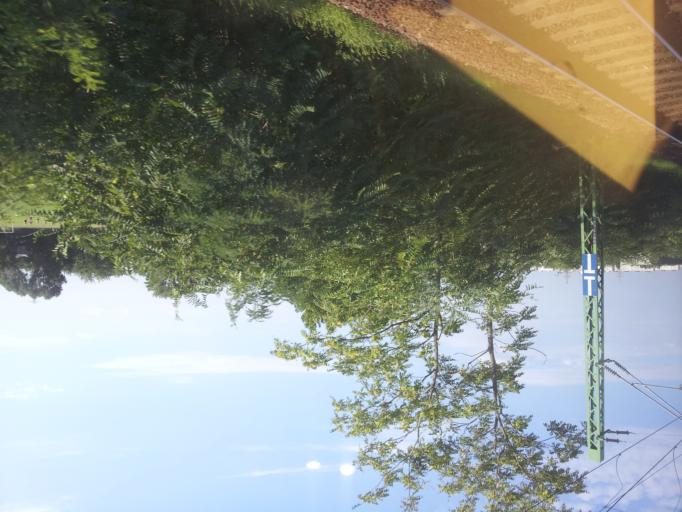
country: HU
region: Budapest
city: Budapest XIX. keruelet
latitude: 47.4711
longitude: 19.1318
